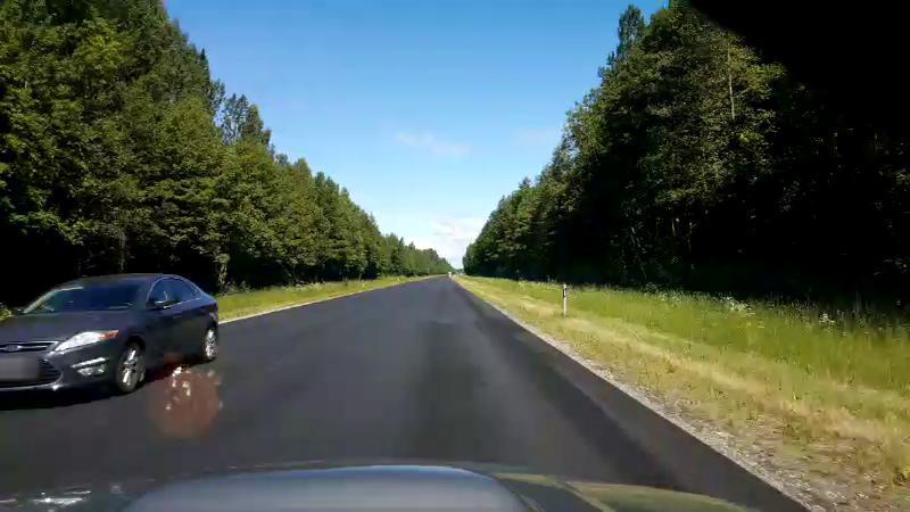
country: LV
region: Salacgrivas
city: Ainazi
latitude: 57.9466
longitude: 24.4346
